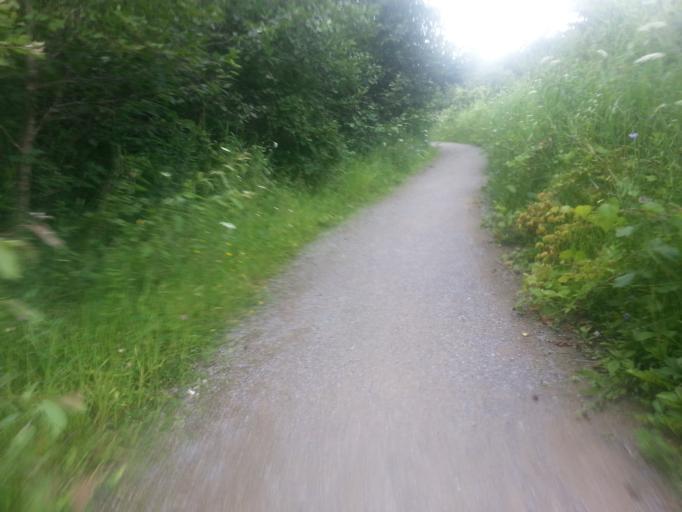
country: CA
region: Ontario
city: Bells Corners
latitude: 45.3294
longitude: -75.9275
